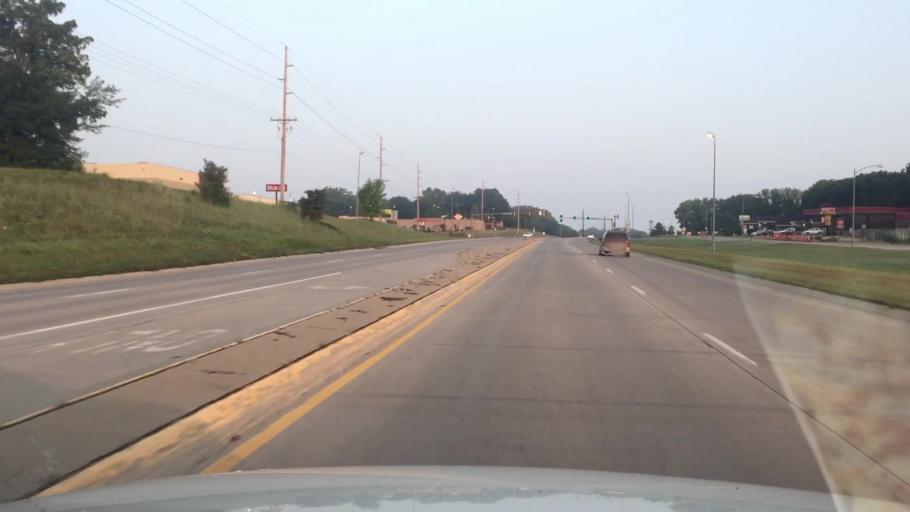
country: US
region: Iowa
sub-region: Warren County
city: Carlisle
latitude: 41.4977
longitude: -93.4952
